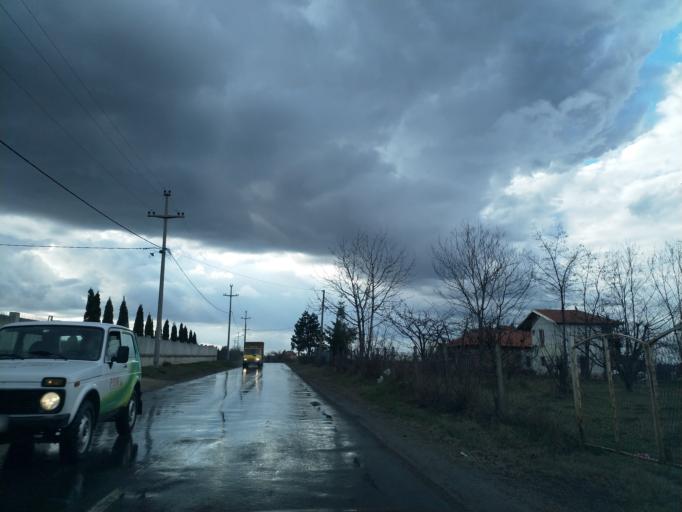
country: RS
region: Central Serbia
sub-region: Belgrade
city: Grocka
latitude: 44.6471
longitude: 20.7559
